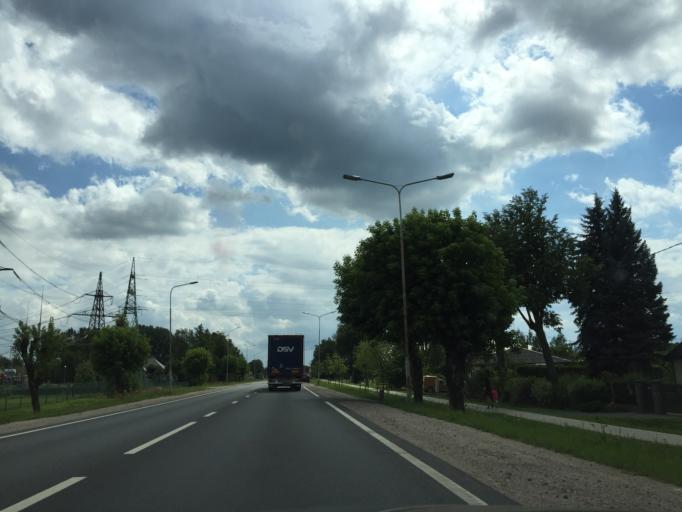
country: LV
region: Jelgava
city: Jelgava
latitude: 56.6281
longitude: 23.7257
